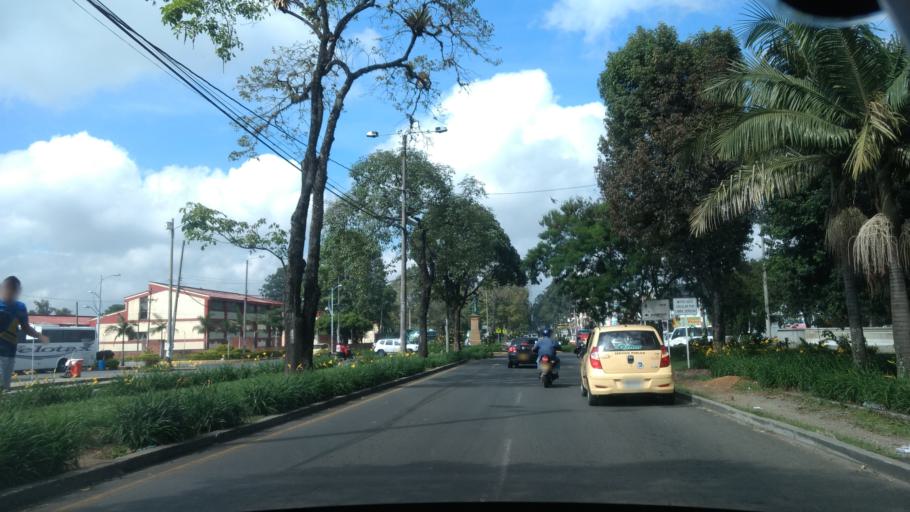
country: CO
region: Cauca
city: Popayan
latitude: 2.4502
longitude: -76.6087
